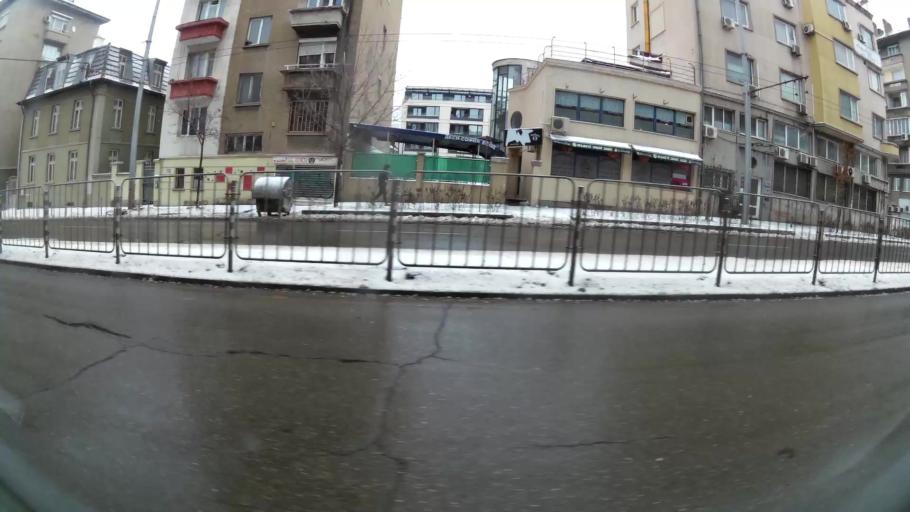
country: BG
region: Sofia-Capital
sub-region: Stolichna Obshtina
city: Sofia
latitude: 42.7001
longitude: 23.3344
